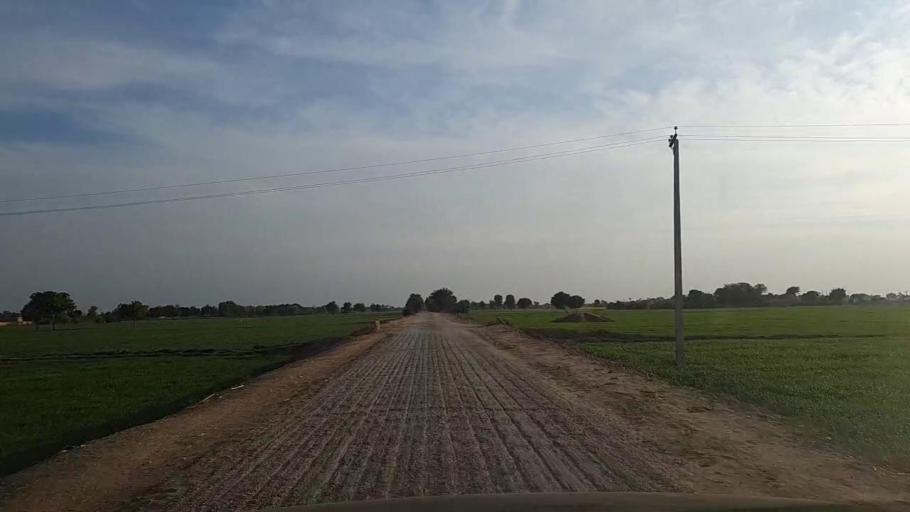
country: PK
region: Sindh
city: Jam Sahib
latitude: 26.4427
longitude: 68.5717
